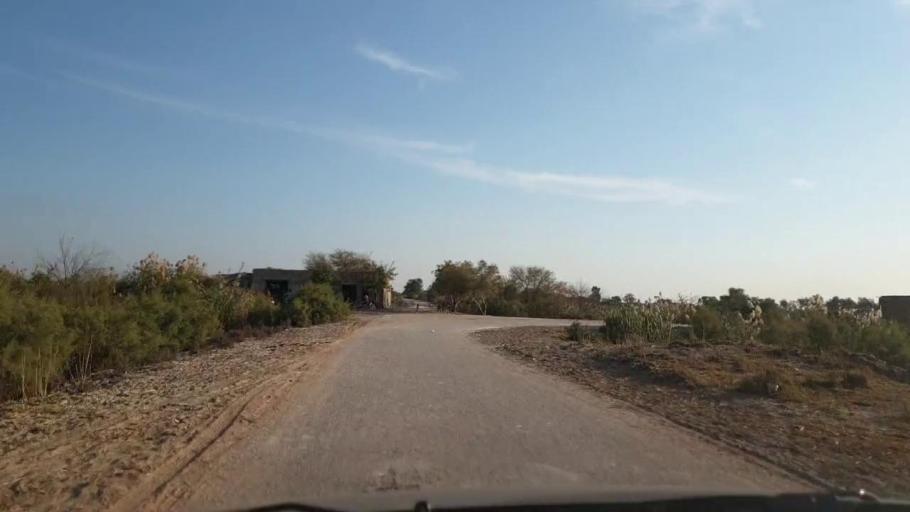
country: PK
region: Sindh
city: Khadro
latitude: 26.2038
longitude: 68.7476
